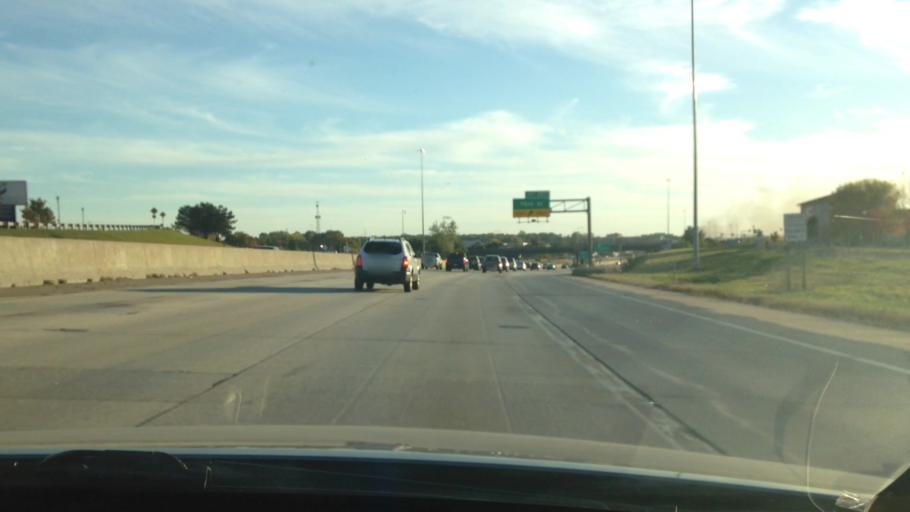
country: US
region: Kansas
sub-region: Johnson County
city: Merriam
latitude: 38.9959
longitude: -94.6959
